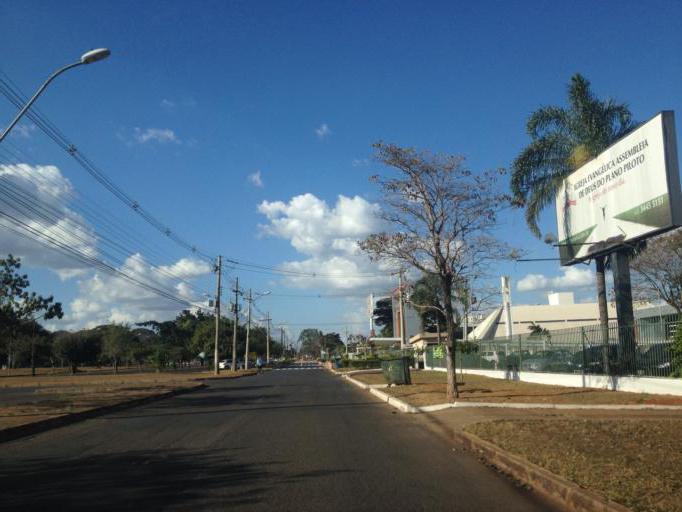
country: BR
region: Federal District
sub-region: Brasilia
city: Brasilia
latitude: -15.8296
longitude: -47.9058
